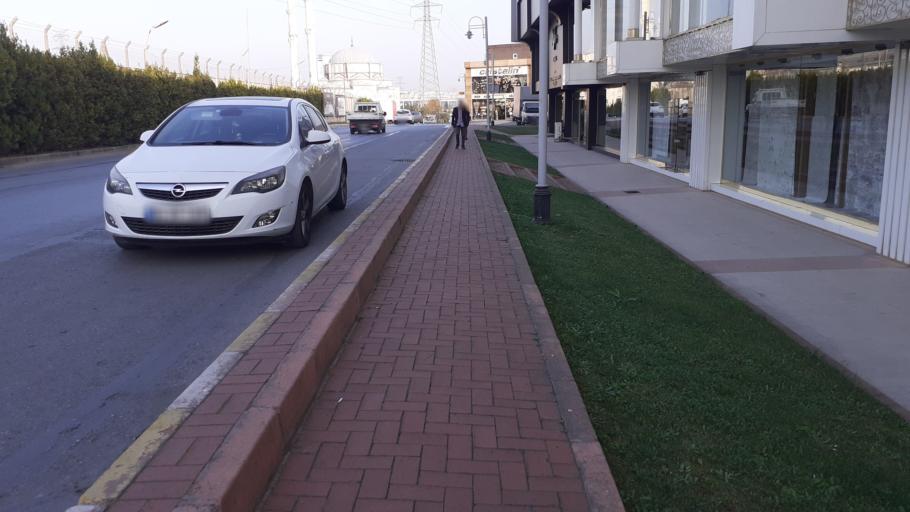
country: TR
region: Istanbul
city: Basaksehir
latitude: 41.0667
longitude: 28.7911
